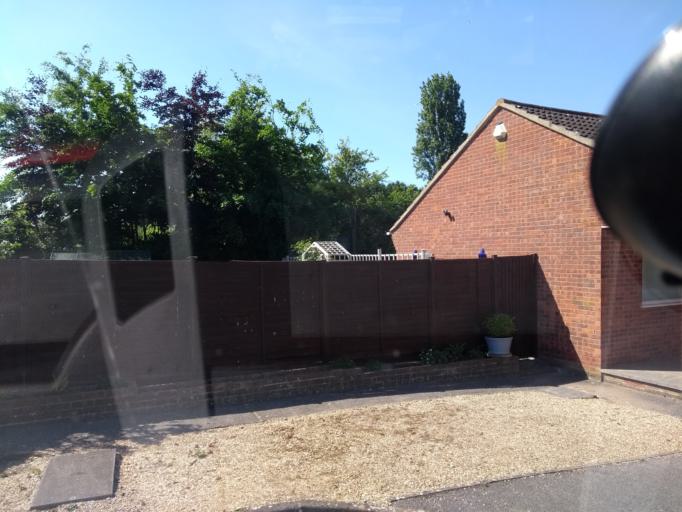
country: GB
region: England
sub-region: Somerset
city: Bridgwater
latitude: 51.1139
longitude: -2.9965
